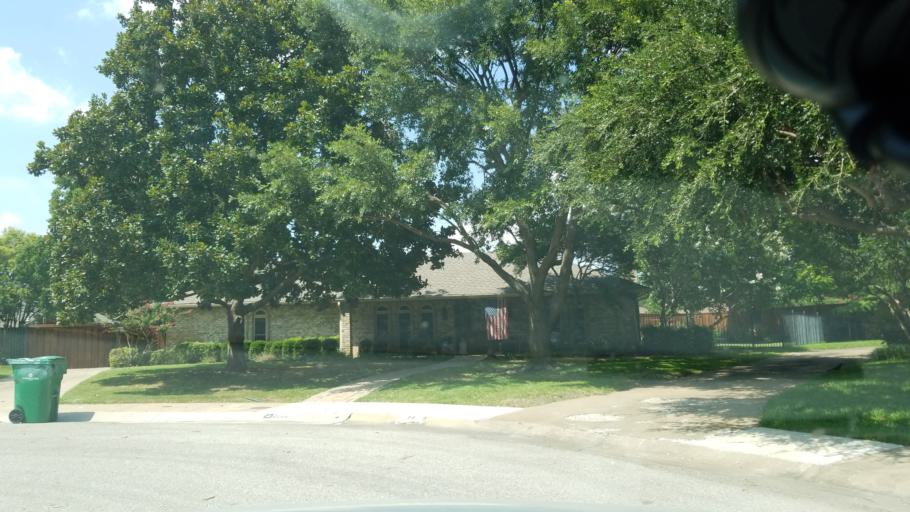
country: US
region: Texas
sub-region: Dallas County
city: Carrollton
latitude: 32.9634
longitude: -96.8610
